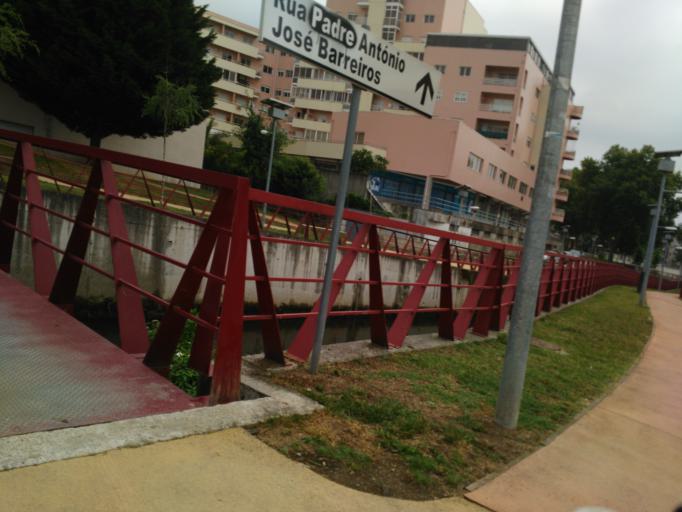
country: PT
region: Braga
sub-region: Braga
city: Braga
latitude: 41.5484
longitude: -8.4088
